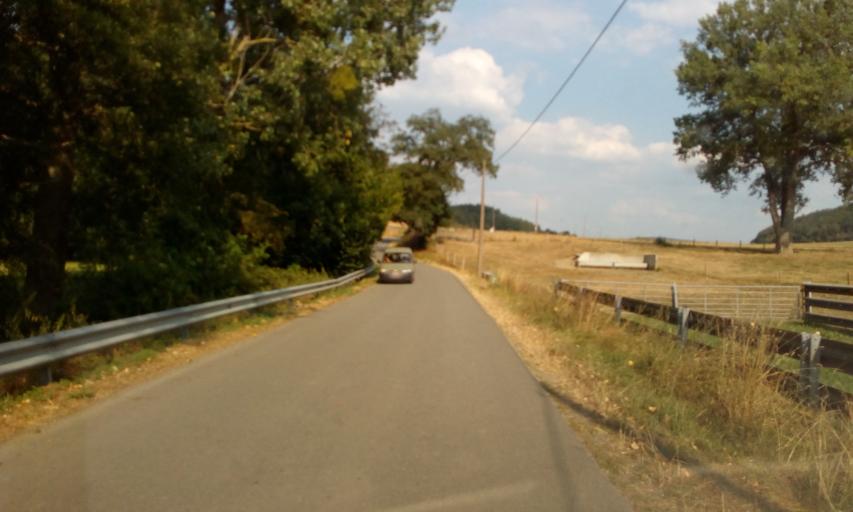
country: BE
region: Wallonia
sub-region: Province du Luxembourg
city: Tellin
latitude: 50.1115
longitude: 5.1694
